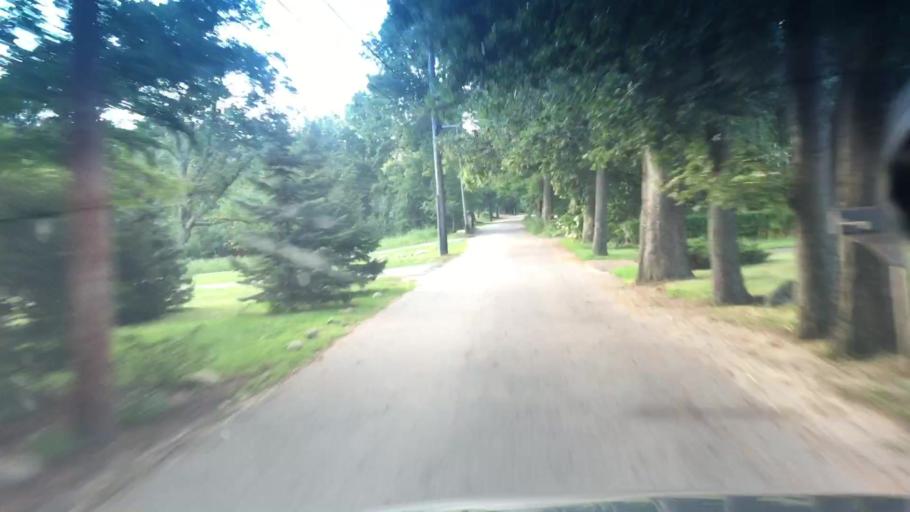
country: US
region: Massachusetts
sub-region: Norfolk County
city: Millis
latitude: 42.1571
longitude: -71.3658
